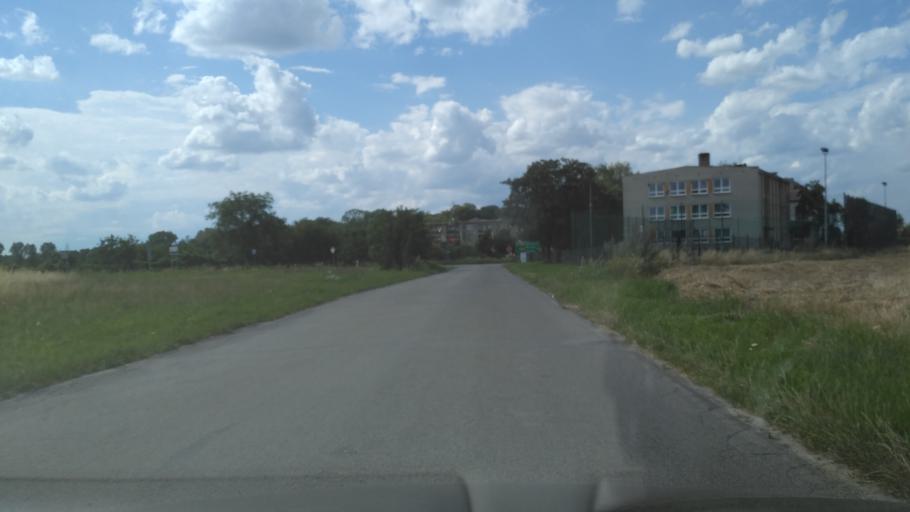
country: PL
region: Lublin Voivodeship
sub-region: Powiat leczynski
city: Milejow
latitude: 51.1881
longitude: 22.9436
